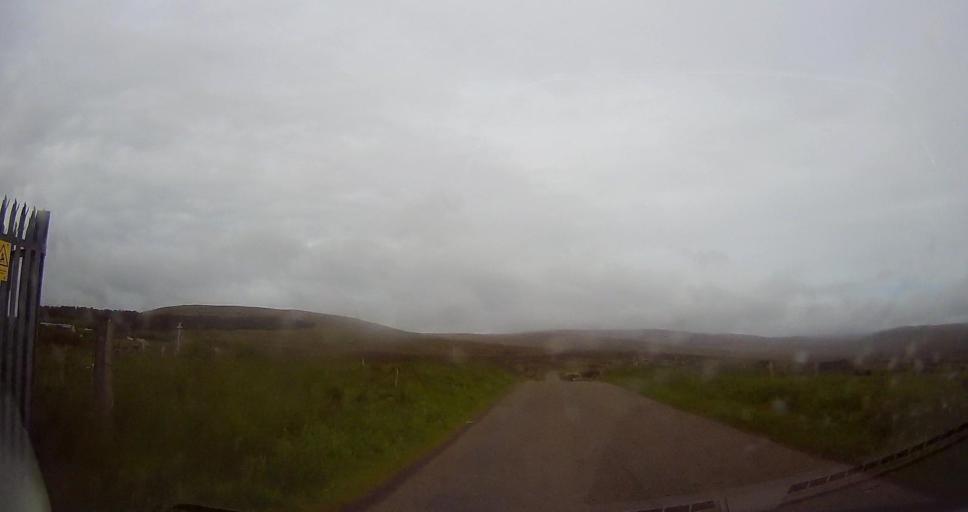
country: GB
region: Scotland
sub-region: Orkney Islands
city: Stromness
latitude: 58.8336
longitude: -3.2079
